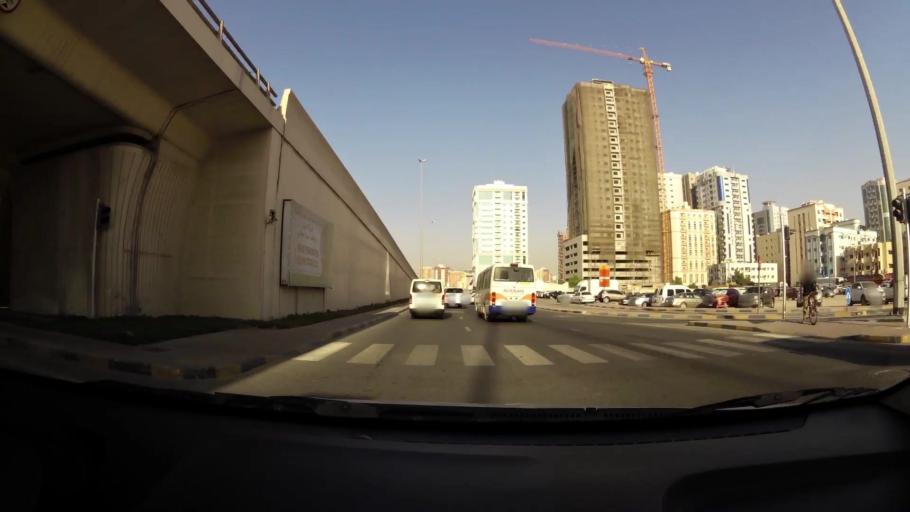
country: AE
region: Ajman
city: Ajman
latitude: 25.3896
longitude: 55.4550
